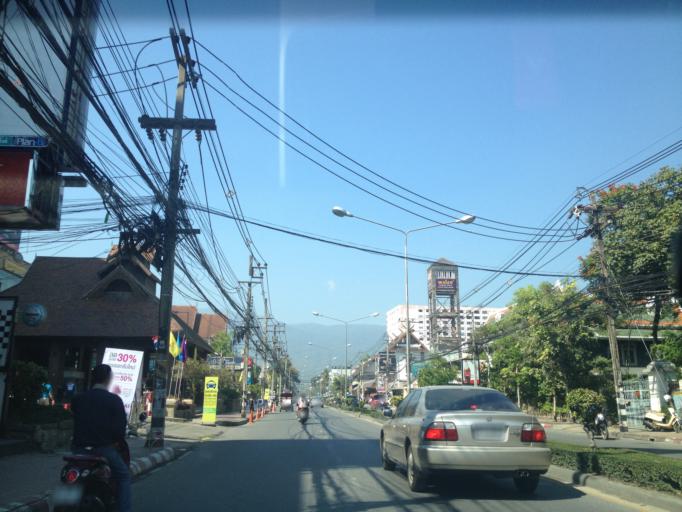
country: TH
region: Chiang Mai
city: Chiang Mai
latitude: 18.7966
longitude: 98.9767
